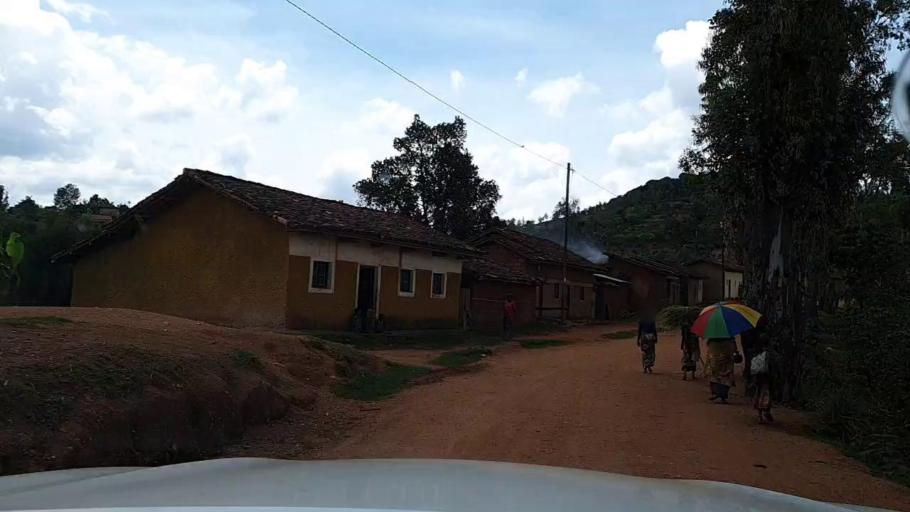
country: RW
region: Southern Province
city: Butare
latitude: -2.7531
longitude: 29.7569
